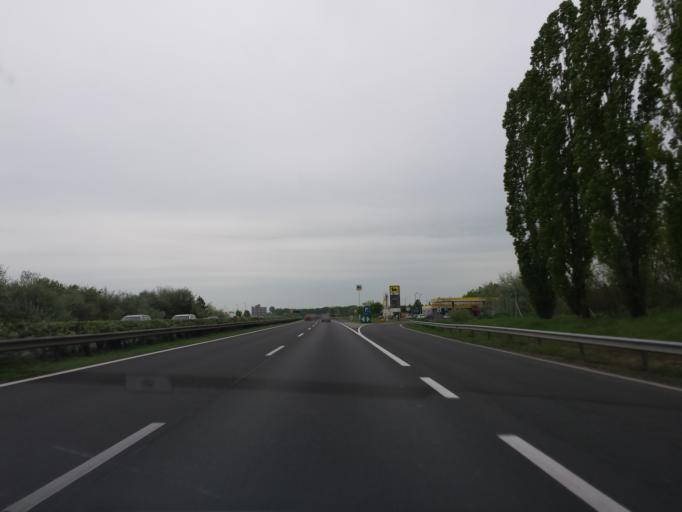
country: HU
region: Pest
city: Zsambek
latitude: 47.5107
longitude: 18.7400
